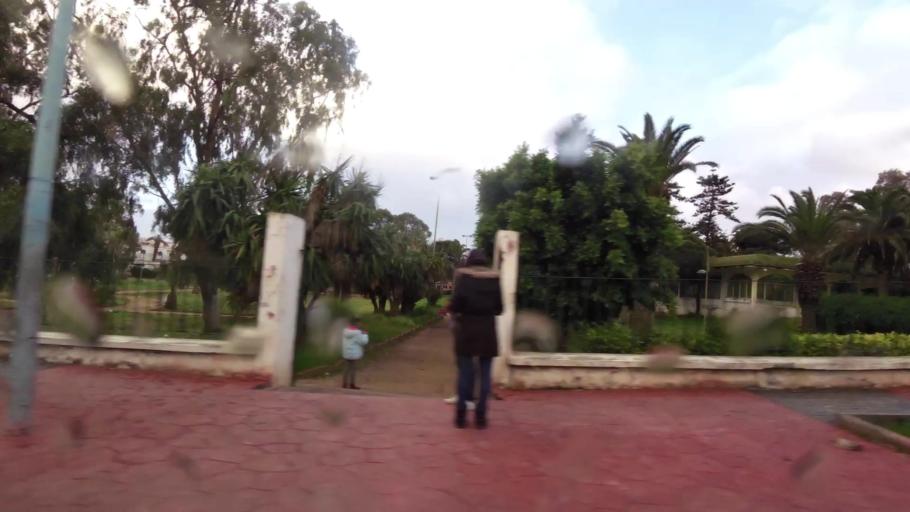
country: MA
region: Doukkala-Abda
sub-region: El-Jadida
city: El Jadida
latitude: 33.2468
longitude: -8.5047
